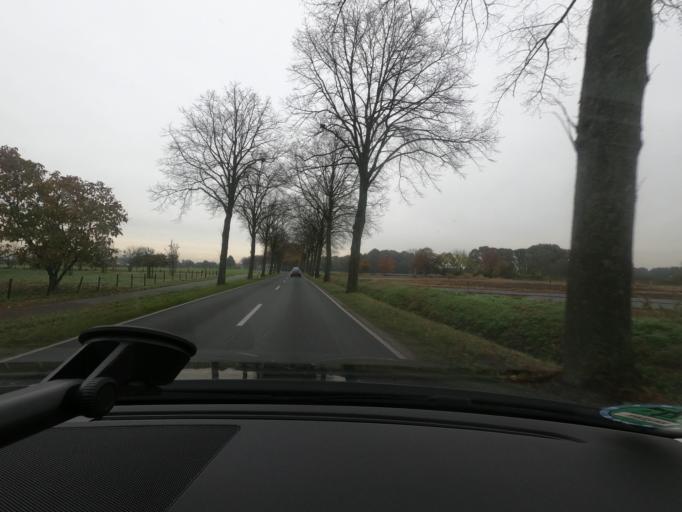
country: DE
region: North Rhine-Westphalia
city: Geldern
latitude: 51.5535
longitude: 6.2968
